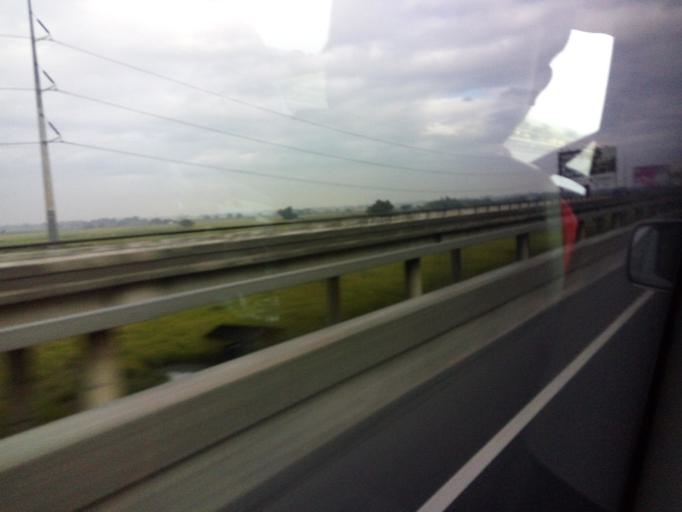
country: PH
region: Central Luzon
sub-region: Province of Pampanga
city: Balucuc
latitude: 14.9288
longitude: 120.7991
